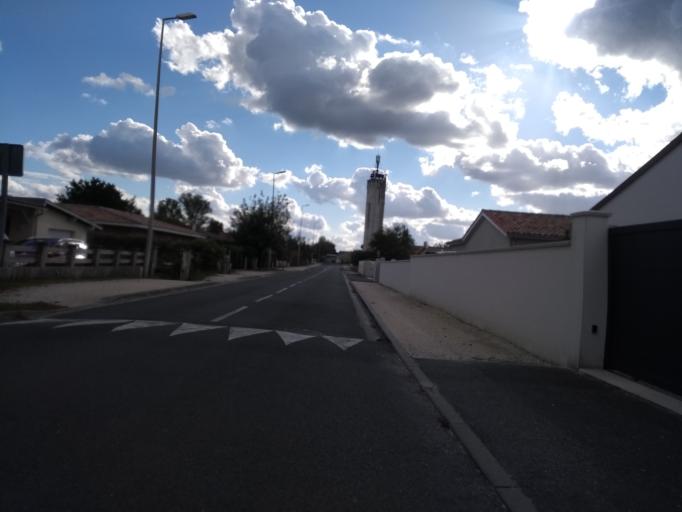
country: FR
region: Aquitaine
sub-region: Departement de la Gironde
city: Cestas
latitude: 44.7427
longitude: -0.6595
